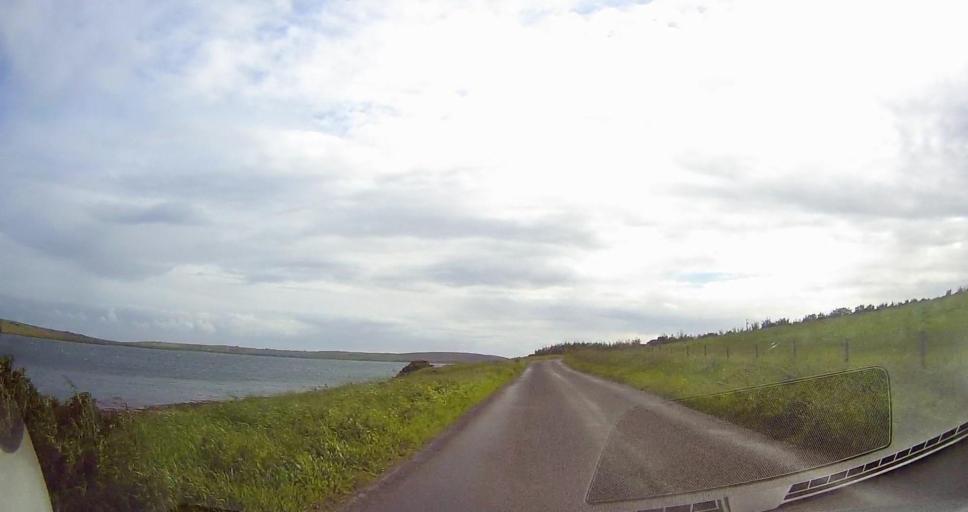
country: GB
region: Scotland
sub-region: Orkney Islands
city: Stromness
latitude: 58.8053
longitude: -3.2190
